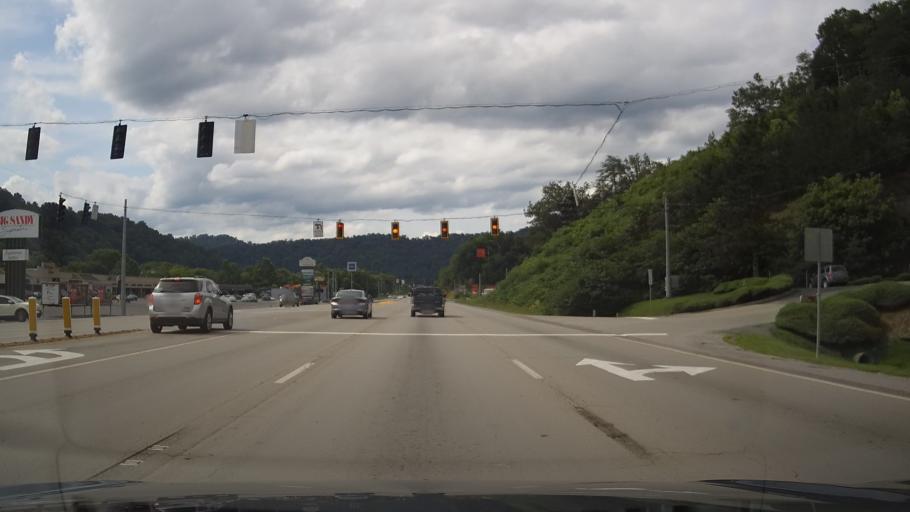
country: US
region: Kentucky
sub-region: Pike County
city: Coal Run Village
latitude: 37.5261
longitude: -82.5736
